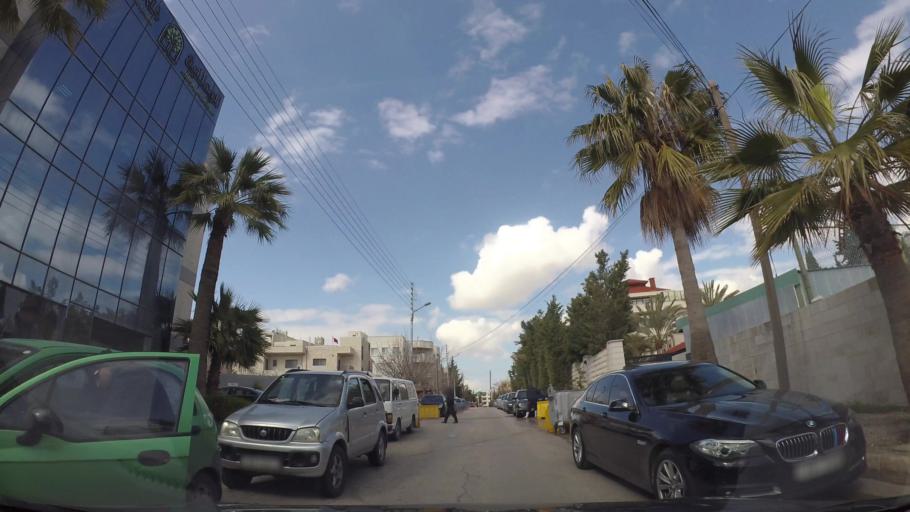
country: JO
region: Amman
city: Amman
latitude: 31.9719
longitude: 35.8948
